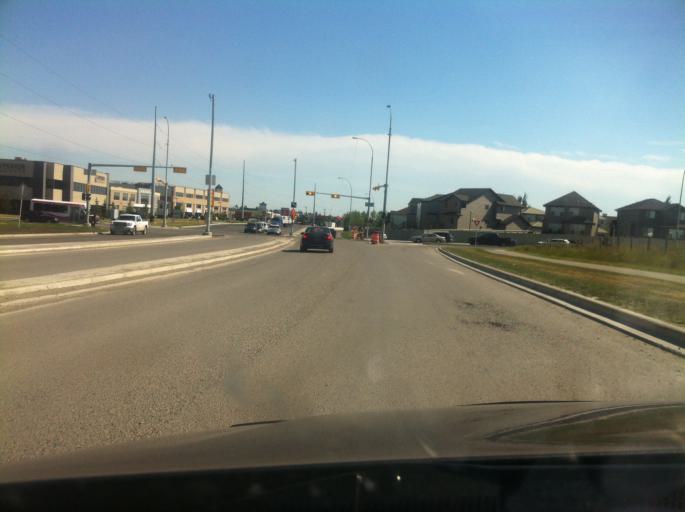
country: CA
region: Alberta
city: Calgary
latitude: 50.9574
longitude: -114.0017
